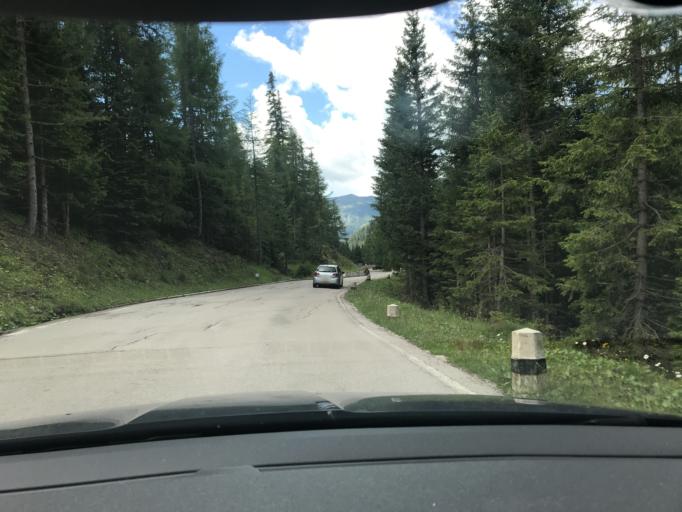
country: IT
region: Veneto
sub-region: Provincia di Belluno
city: Livinallongo del Col di Lana
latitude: 46.5077
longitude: 11.9988
